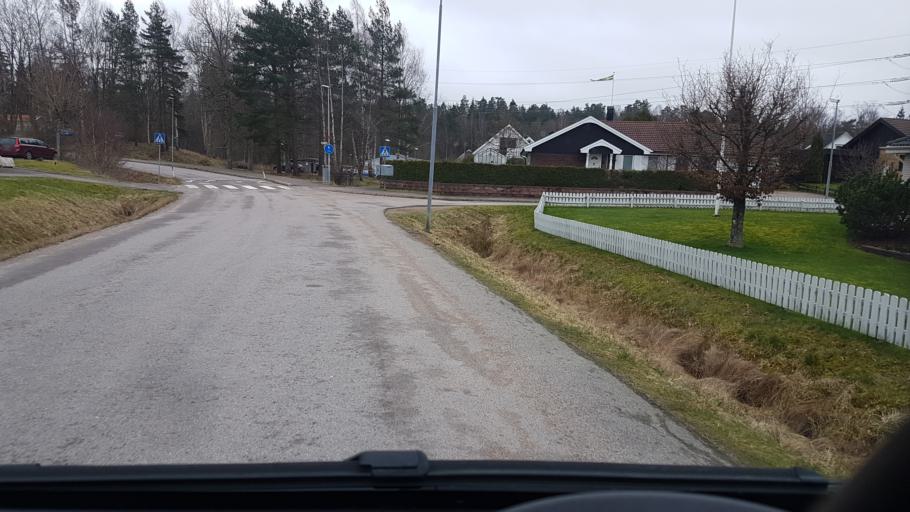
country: SE
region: Vaestra Goetaland
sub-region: Lerums Kommun
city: Stenkullen
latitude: 57.8080
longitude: 12.3382
